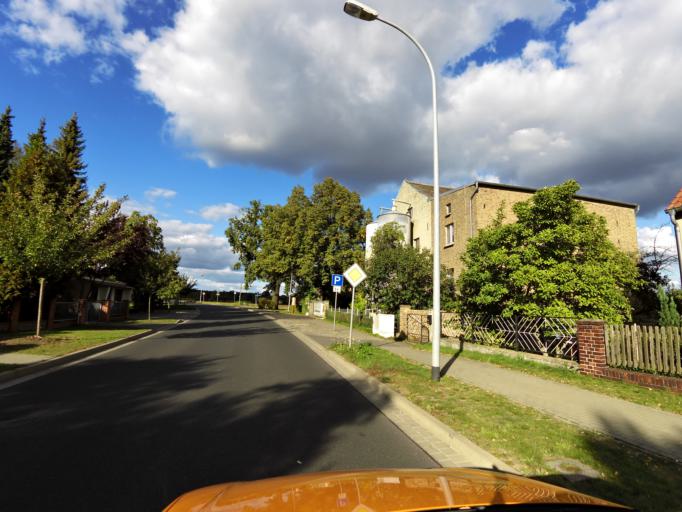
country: DE
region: Brandenburg
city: Luckenwalde
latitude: 52.1044
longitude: 13.1746
